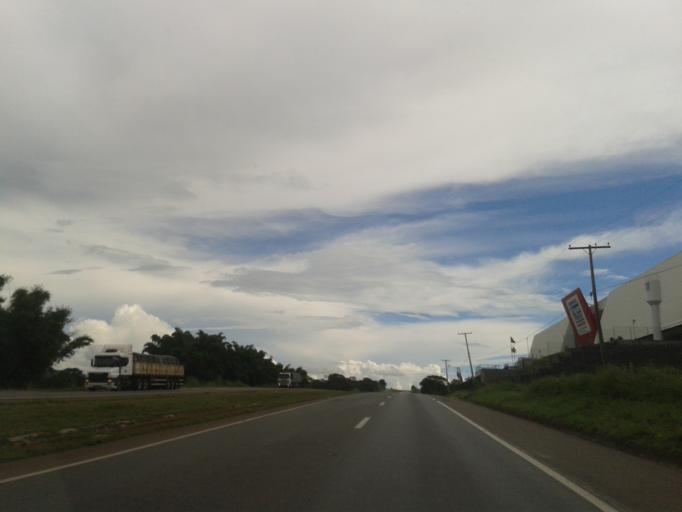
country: BR
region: Goias
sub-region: Aparecida De Goiania
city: Aparecida de Goiania
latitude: -16.8546
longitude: -49.2480
